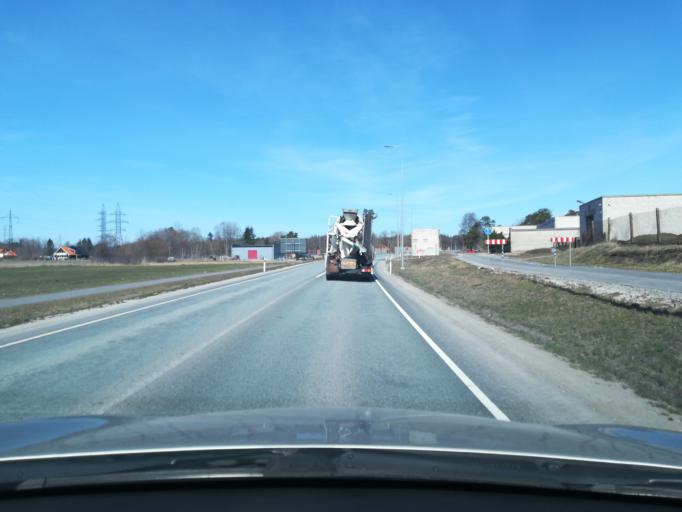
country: EE
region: Harju
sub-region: Saue vald
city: Laagri
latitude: 59.3478
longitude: 24.5993
